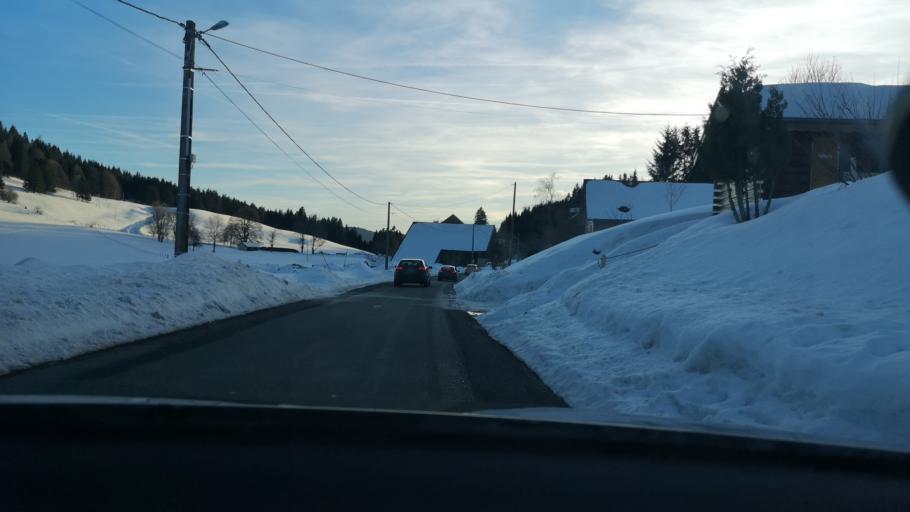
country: FR
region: Franche-Comte
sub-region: Departement du Doubs
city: Gilley
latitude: 46.9659
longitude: 6.4742
